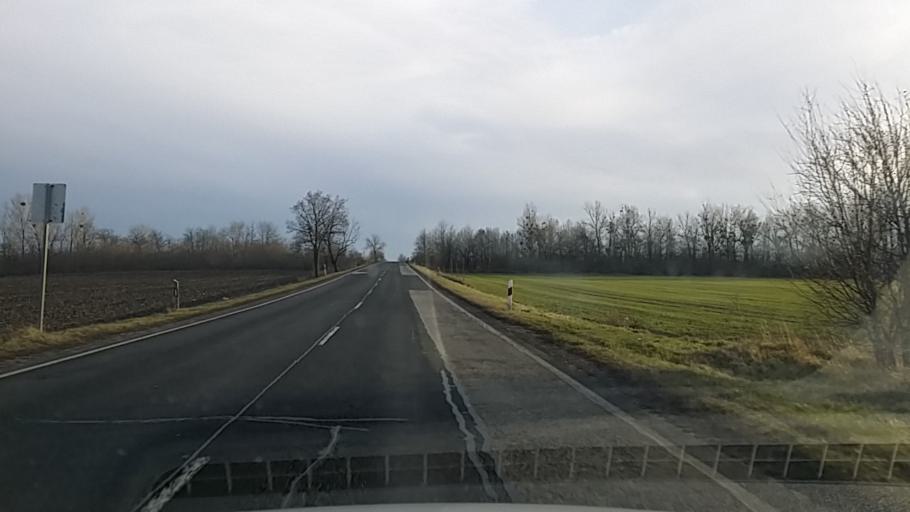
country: HU
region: Komarom-Esztergom
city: Kisber
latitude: 47.4986
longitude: 18.0475
